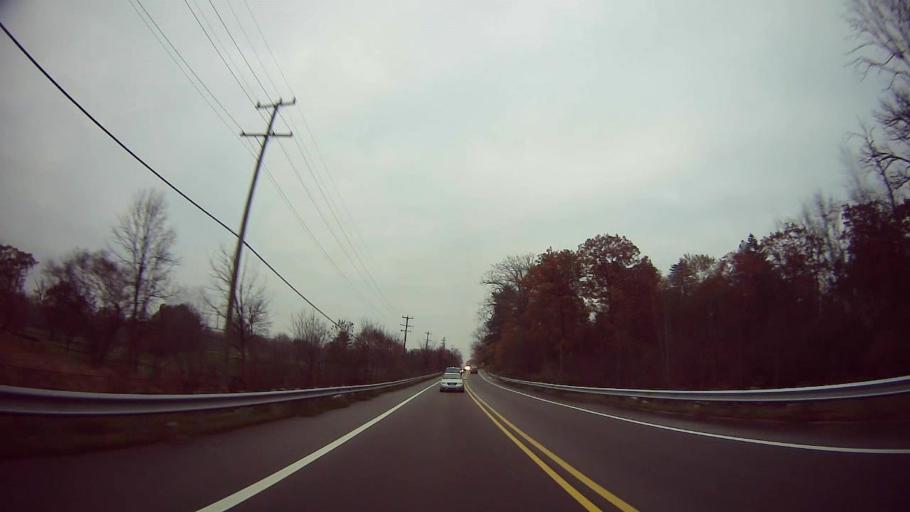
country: US
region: Michigan
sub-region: Oakland County
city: Birmingham
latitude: 42.5605
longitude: -83.2149
